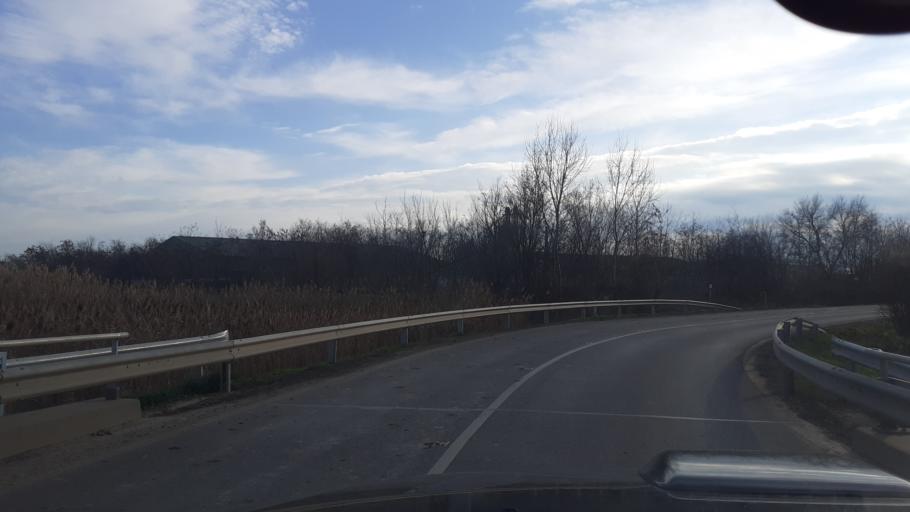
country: HU
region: Bacs-Kiskun
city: Tass
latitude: 47.0193
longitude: 19.0428
